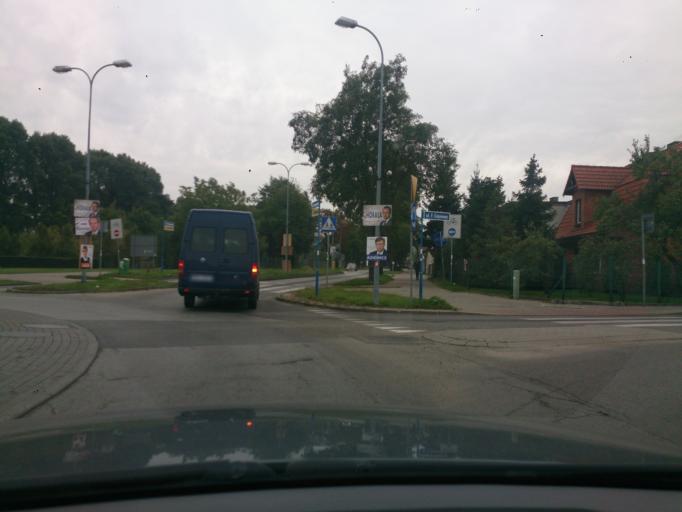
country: PL
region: Pomeranian Voivodeship
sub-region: Powiat wejherowski
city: Rumia
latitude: 54.5785
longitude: 18.3977
